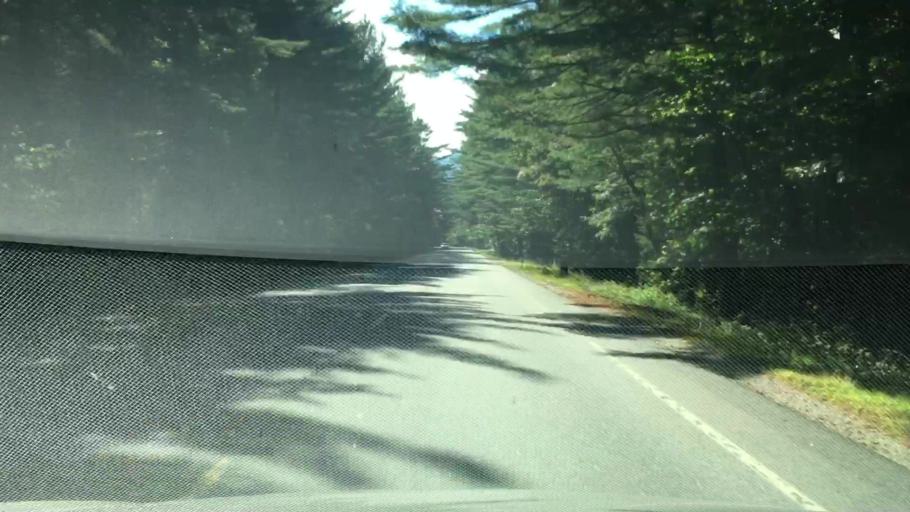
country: US
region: New Hampshire
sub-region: Carroll County
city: Tamworth
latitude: 43.9966
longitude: -71.3656
